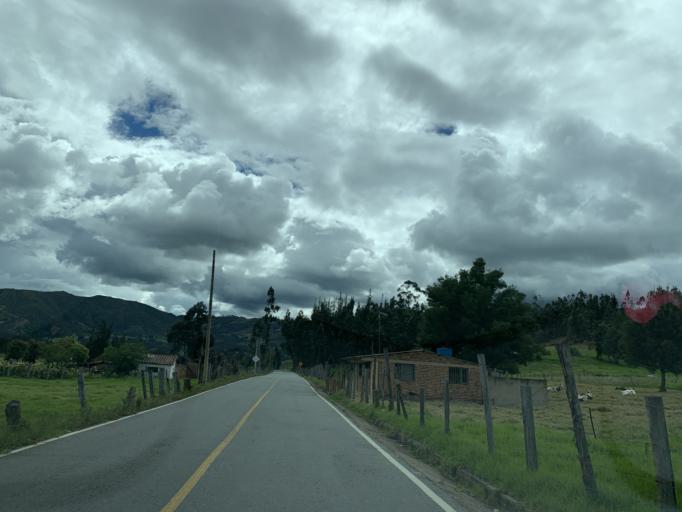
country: CO
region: Boyaca
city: Floresta
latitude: 5.8532
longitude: -72.9288
